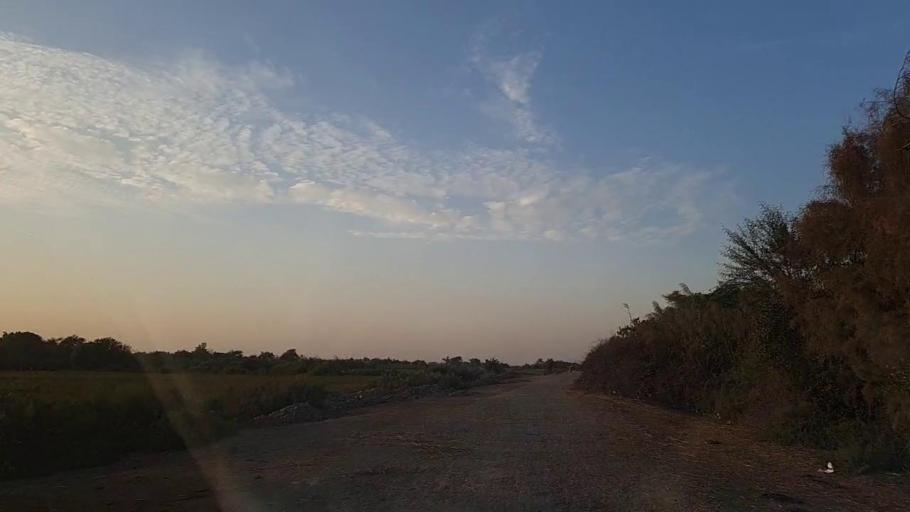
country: PK
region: Sindh
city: Chuhar Jamali
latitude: 24.4581
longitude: 68.1151
